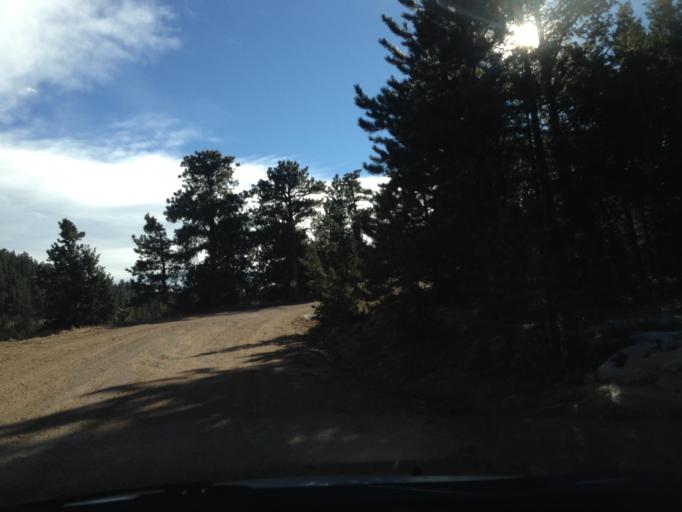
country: US
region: Colorado
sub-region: Boulder County
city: Coal Creek
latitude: 39.9197
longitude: -105.3521
